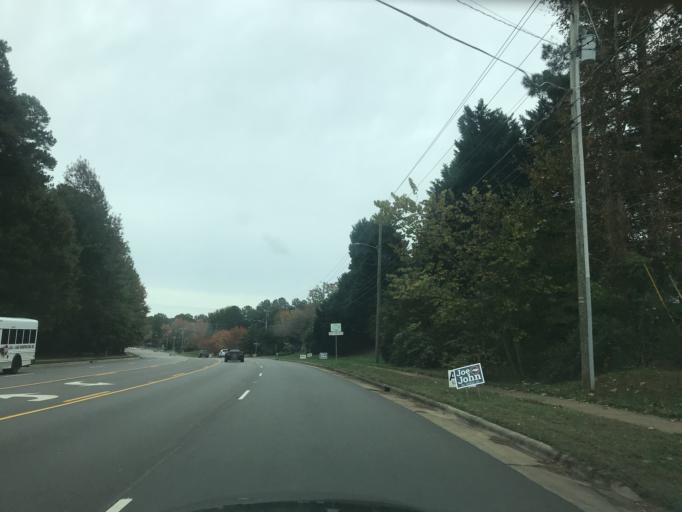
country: US
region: North Carolina
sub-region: Wake County
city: West Raleigh
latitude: 35.8956
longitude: -78.6421
